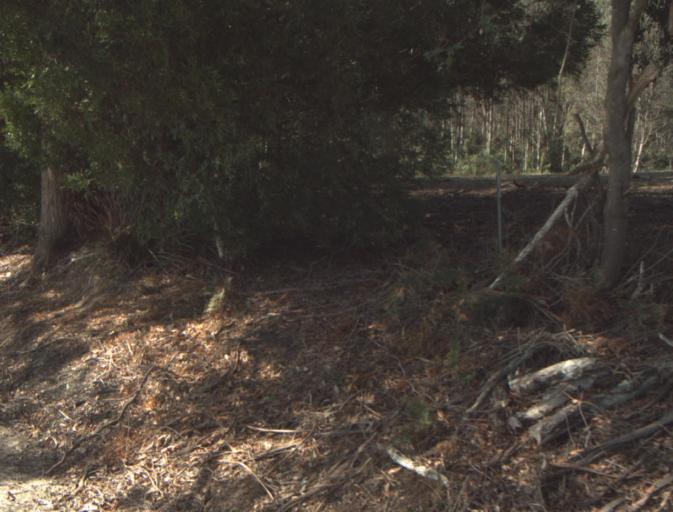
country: AU
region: Tasmania
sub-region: Launceston
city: Mayfield
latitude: -41.2198
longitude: 147.2393
